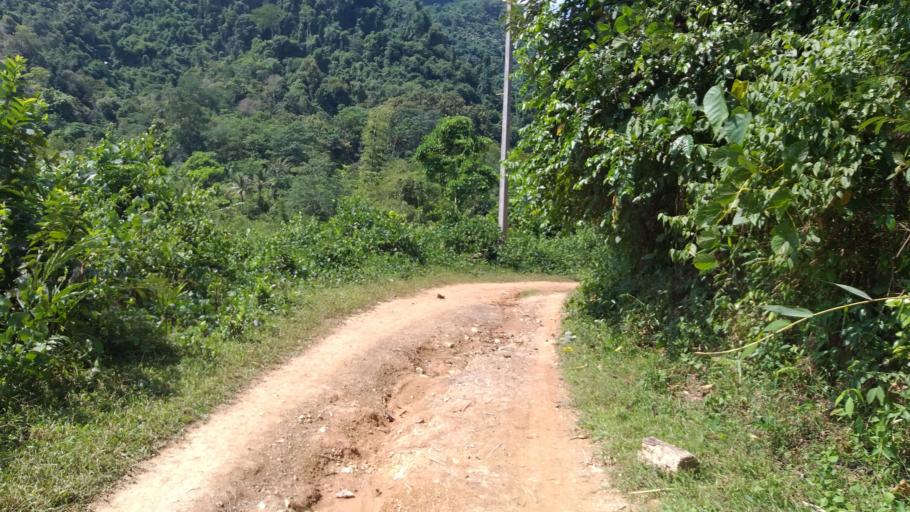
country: LA
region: Phongsali
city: Khoa
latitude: 21.3445
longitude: 102.5358
